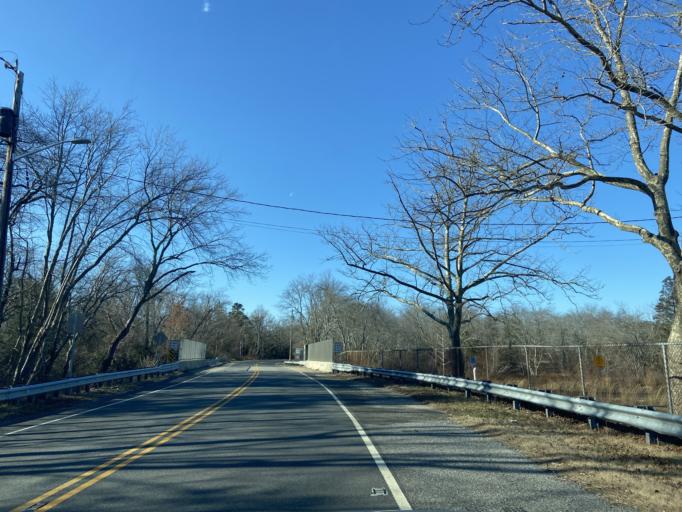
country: US
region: New Jersey
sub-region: Cumberland County
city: Vineland
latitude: 39.4958
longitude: -75.0756
